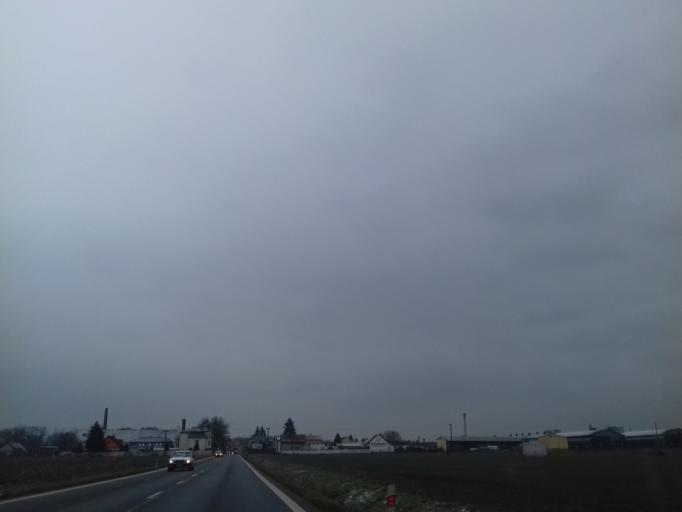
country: CZ
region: Plzensky
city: Stankov
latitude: 49.5618
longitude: 13.0749
